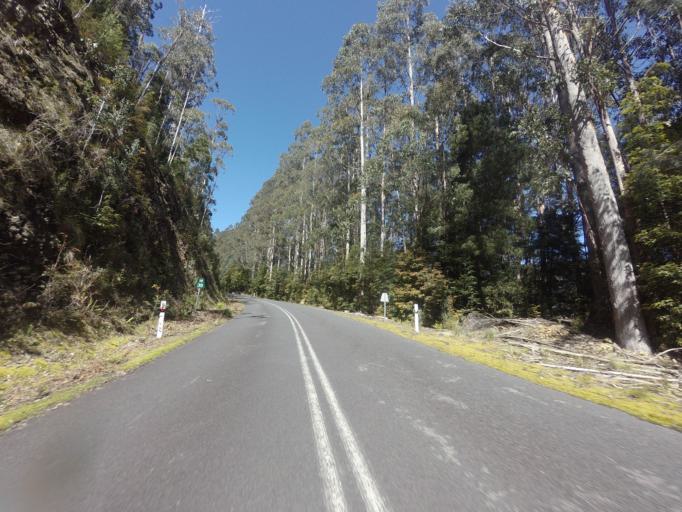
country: AU
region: Tasmania
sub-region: Huon Valley
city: Geeveston
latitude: -42.8200
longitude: 146.3379
